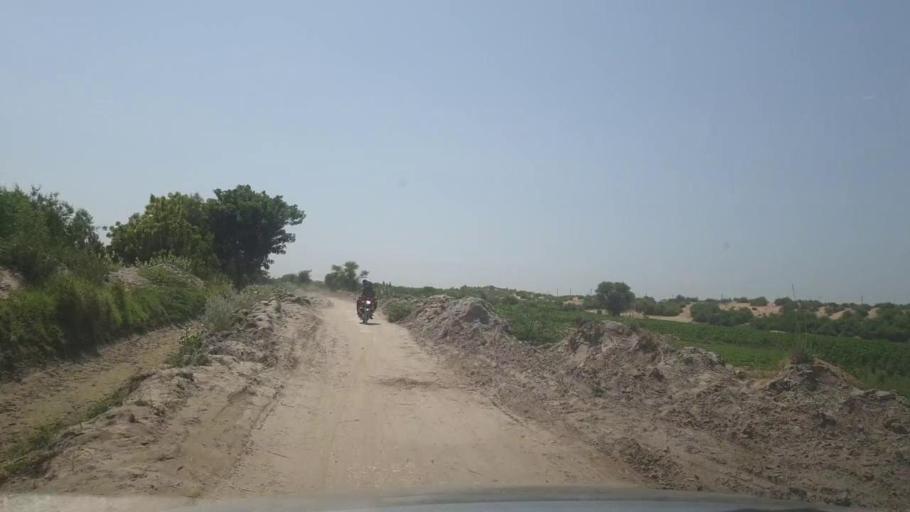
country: PK
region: Sindh
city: Khairpur
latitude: 27.3551
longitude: 69.0412
